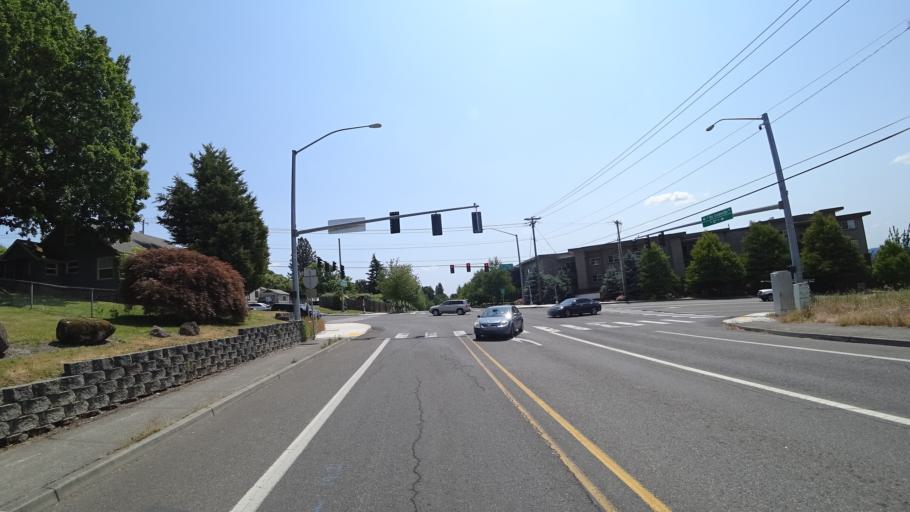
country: US
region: Oregon
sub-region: Multnomah County
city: Lents
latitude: 45.4509
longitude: -122.5687
